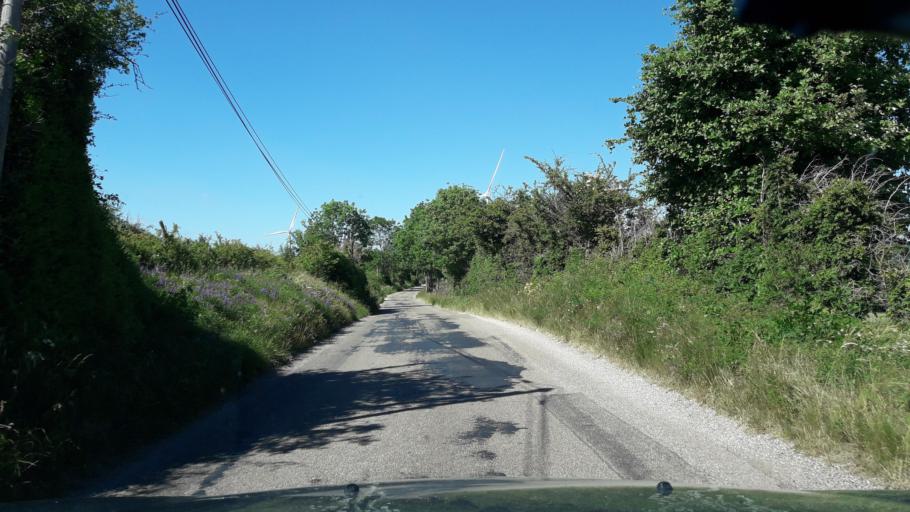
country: FR
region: Rhone-Alpes
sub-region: Departement de l'Ardeche
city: Saint-Priest
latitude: 44.6807
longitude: 4.5587
